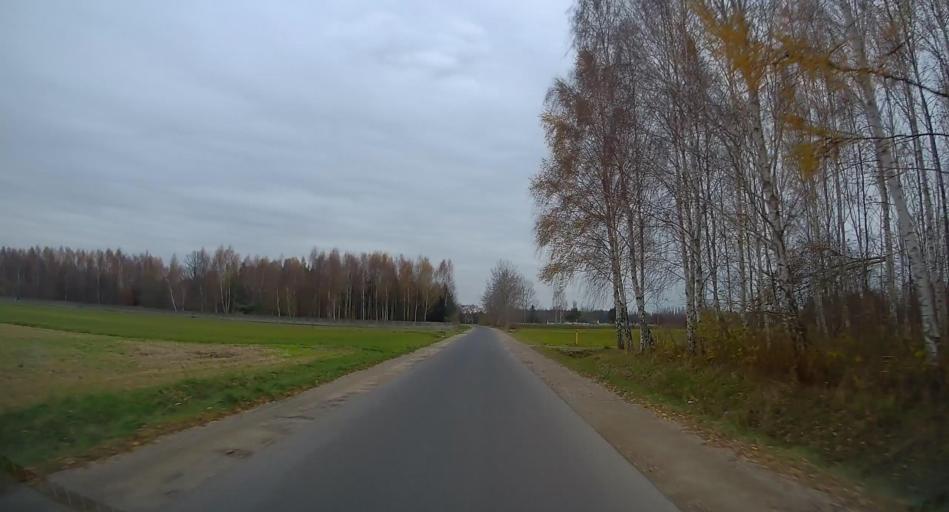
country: PL
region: Lodz Voivodeship
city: Zabia Wola
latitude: 51.9927
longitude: 20.6600
